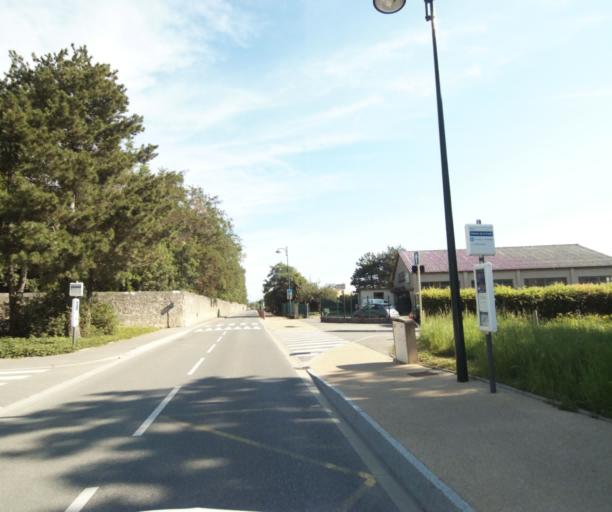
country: FR
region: Rhone-Alpes
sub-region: Departement de la Haute-Savoie
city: Thonon-les-Bains
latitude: 46.3910
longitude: 6.5032
